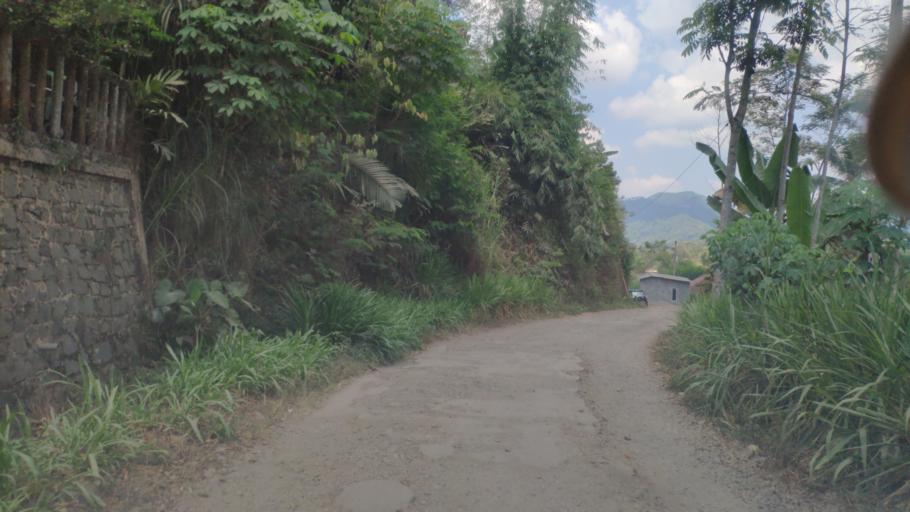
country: ID
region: Central Java
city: Wonosobo
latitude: -7.3221
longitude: 109.6610
